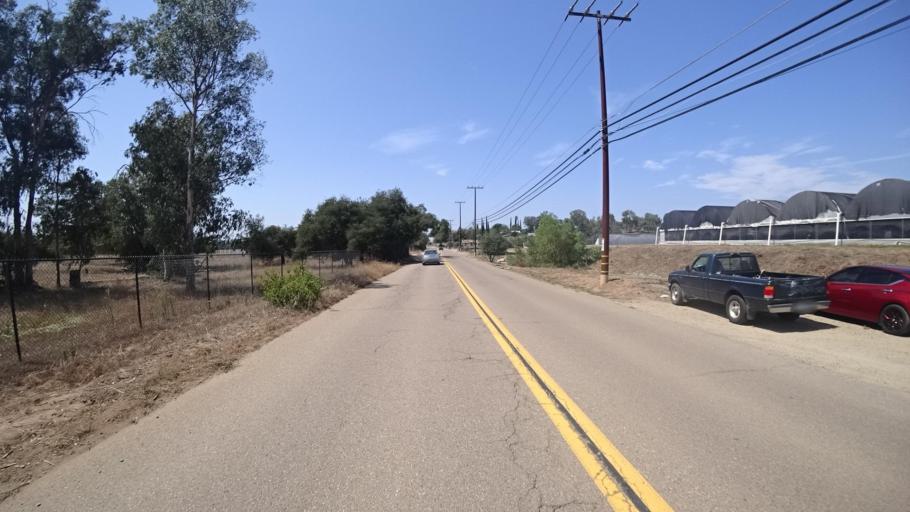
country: US
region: California
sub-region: San Diego County
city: Valley Center
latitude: 33.2421
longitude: -117.0134
